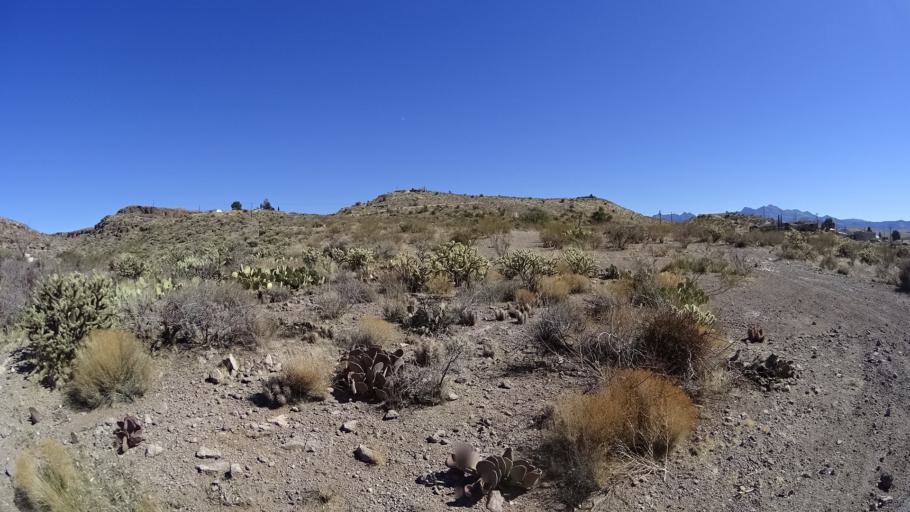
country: US
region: Arizona
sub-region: Mohave County
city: Kingman
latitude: 35.1982
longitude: -114.0607
